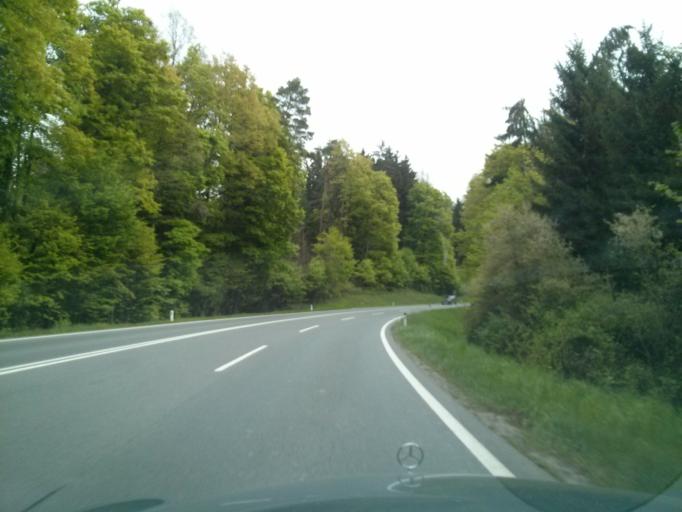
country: AT
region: Burgenland
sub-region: Politischer Bezirk Oberwart
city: Oberwart
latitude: 47.2786
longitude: 16.1630
